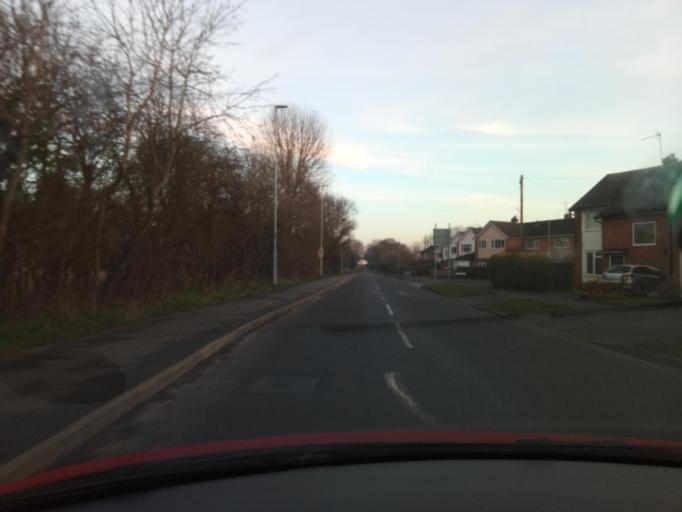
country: GB
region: England
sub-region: Leicestershire
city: Mountsorrel
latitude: 52.7233
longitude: -1.1493
